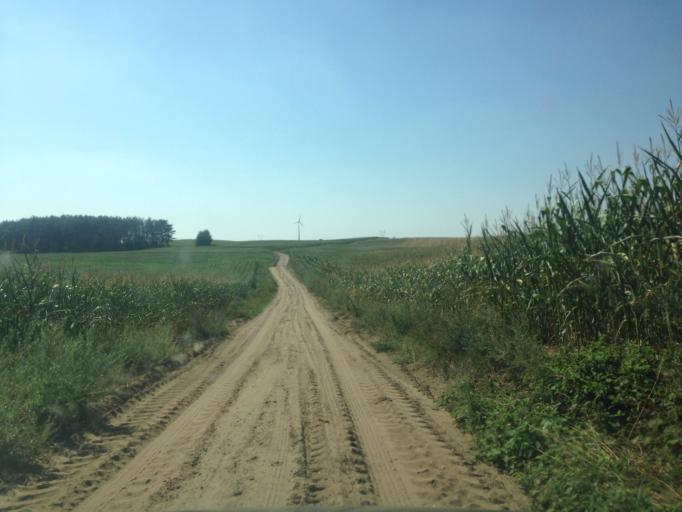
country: PL
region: Kujawsko-Pomorskie
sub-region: Powiat brodnicki
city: Brzozie
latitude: 53.2899
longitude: 19.6854
